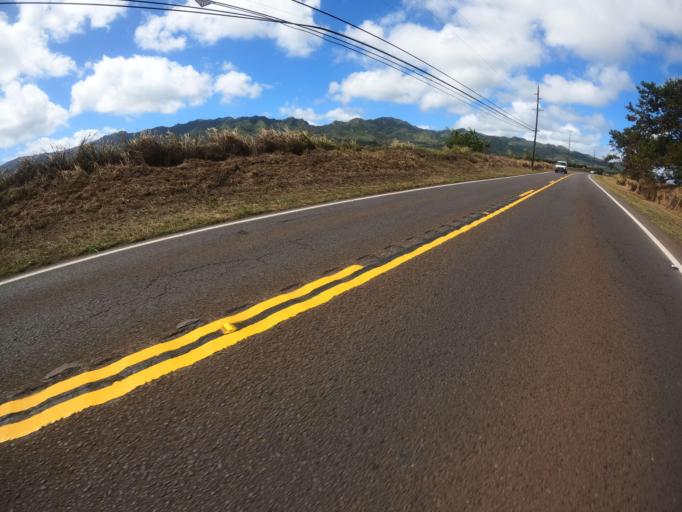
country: US
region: Hawaii
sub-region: Honolulu County
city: Village Park
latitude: 21.4259
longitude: -158.0541
